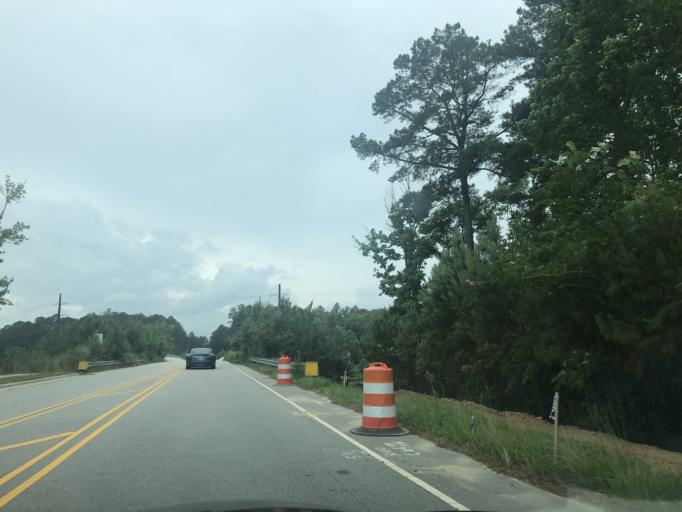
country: US
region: North Carolina
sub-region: Wake County
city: Green Level
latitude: 35.8042
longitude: -78.8904
